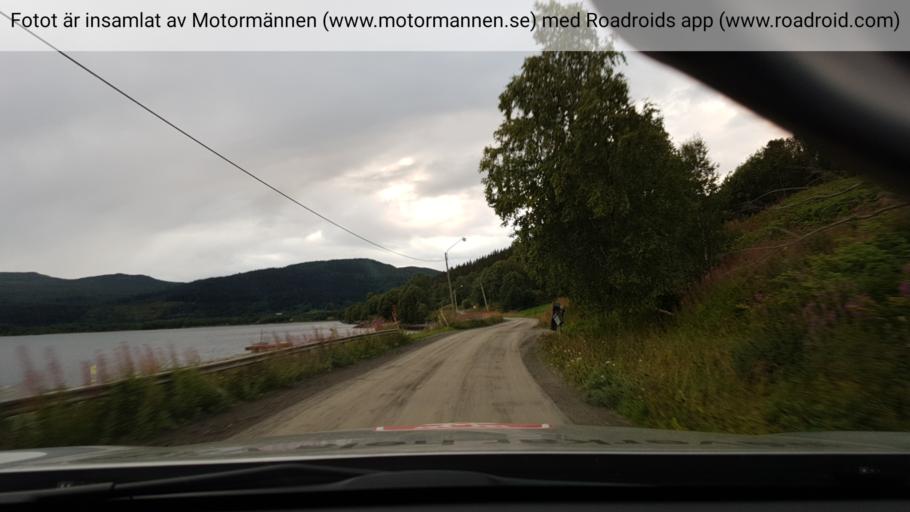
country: NO
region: Nordland
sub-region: Hattfjelldal
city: Hattfjelldal
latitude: 65.6519
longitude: 15.1692
